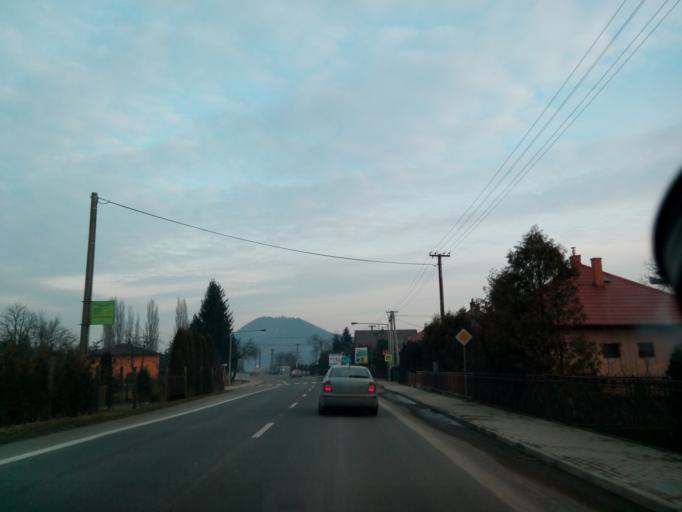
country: SK
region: Presovsky
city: Sabinov
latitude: 49.0687
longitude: 21.1375
